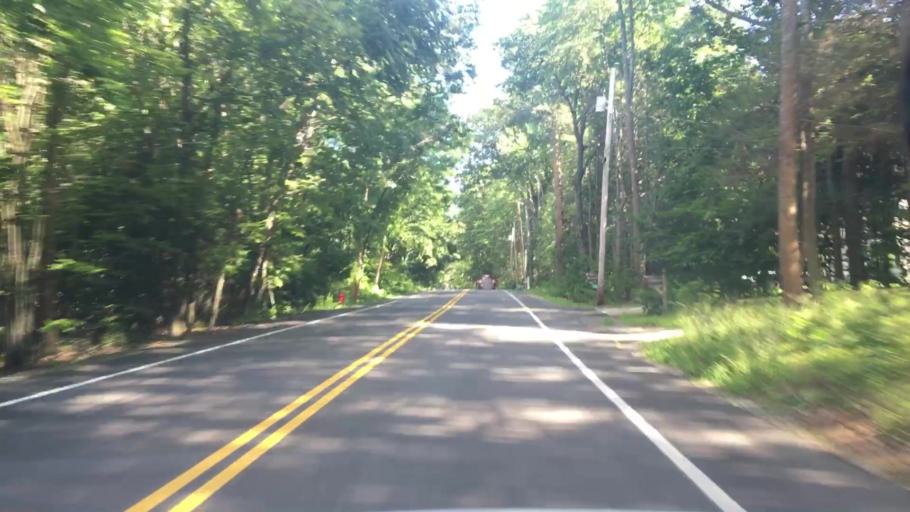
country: US
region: New Hampshire
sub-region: Strafford County
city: Dover
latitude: 43.1641
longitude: -70.8812
